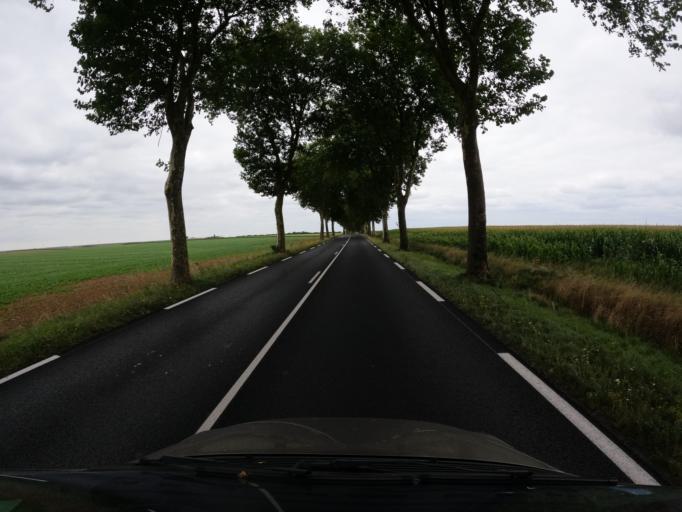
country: FR
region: Pays de la Loire
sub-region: Departement de la Vendee
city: Le Langon
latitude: 46.4994
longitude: -0.9290
